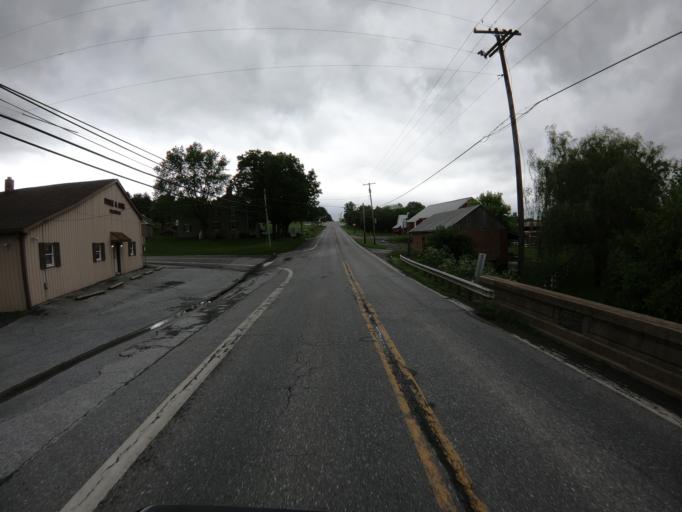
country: US
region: Maryland
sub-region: Frederick County
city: Middletown
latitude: 39.4502
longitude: -77.5624
